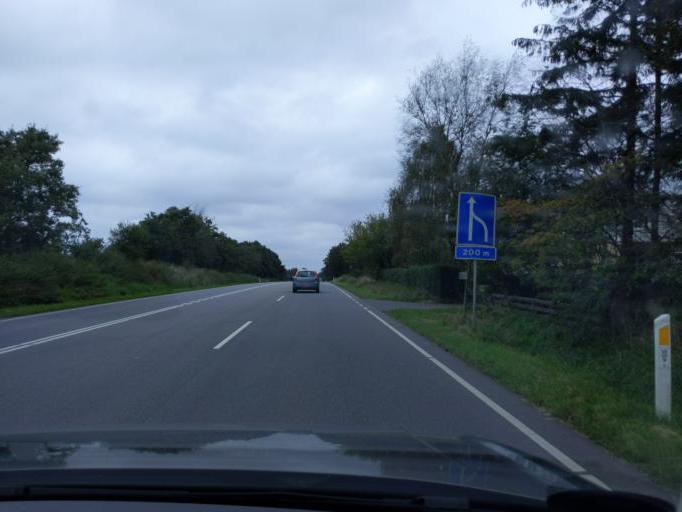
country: DK
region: North Denmark
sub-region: Mariagerfjord Kommune
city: Hobro
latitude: 56.5730
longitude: 9.8168
